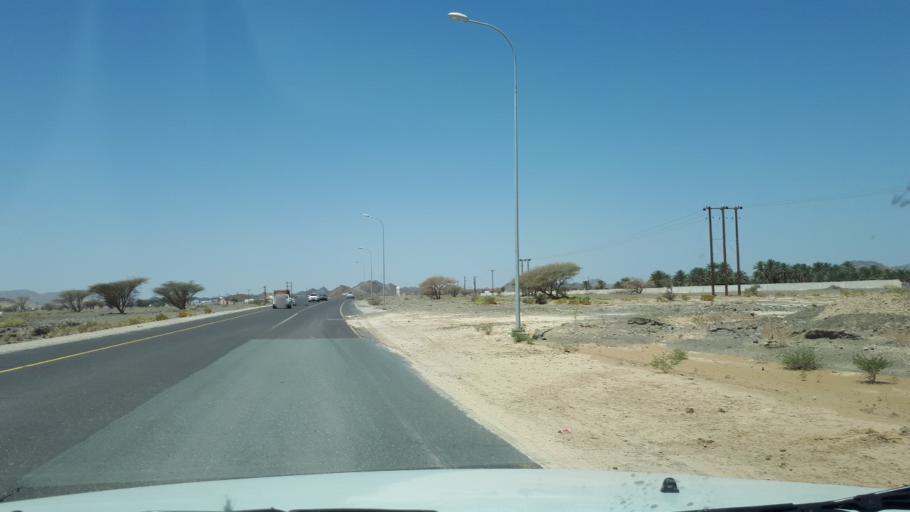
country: OM
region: Ash Sharqiyah
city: Ibra'
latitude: 22.6168
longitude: 58.3978
